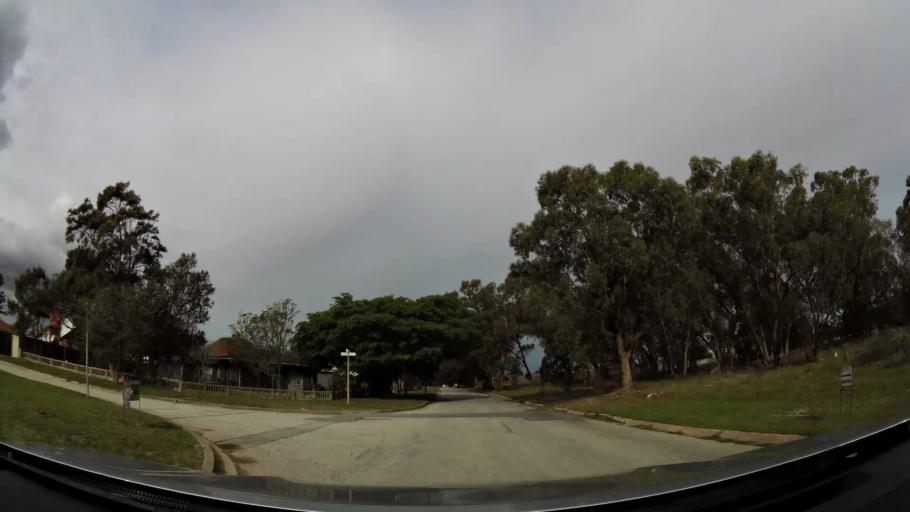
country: ZA
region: Eastern Cape
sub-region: Nelson Mandela Bay Metropolitan Municipality
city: Port Elizabeth
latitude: -33.9354
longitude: 25.4918
